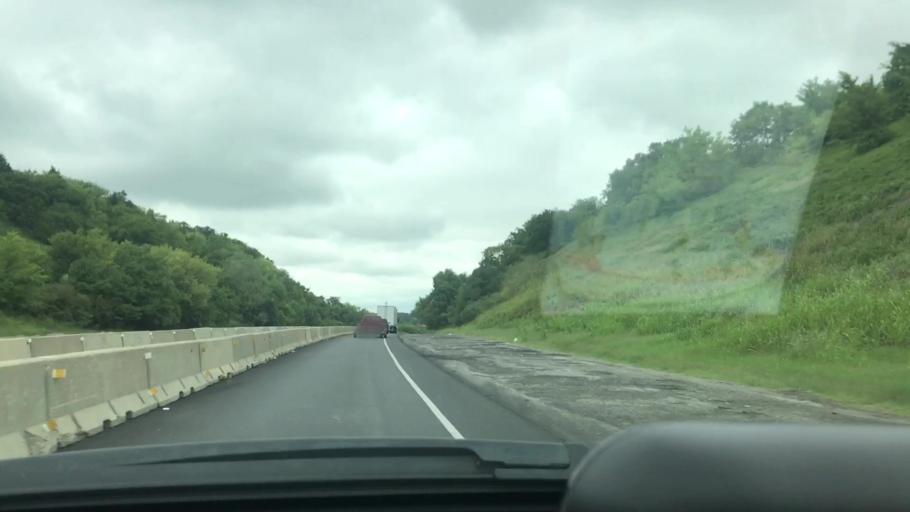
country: US
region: Oklahoma
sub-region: McIntosh County
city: Eufaula
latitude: 35.2713
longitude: -95.5923
